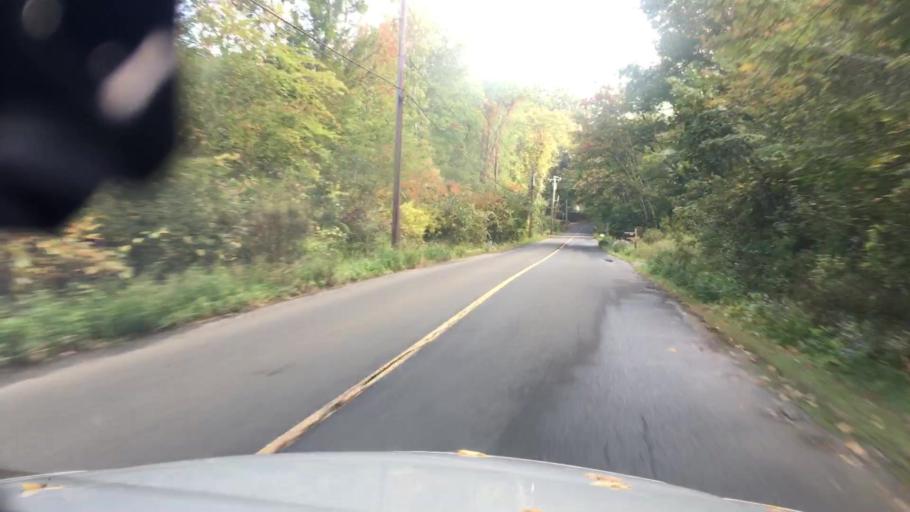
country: US
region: Connecticut
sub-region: Middlesex County
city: Essex Village
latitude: 41.3760
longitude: -72.4102
